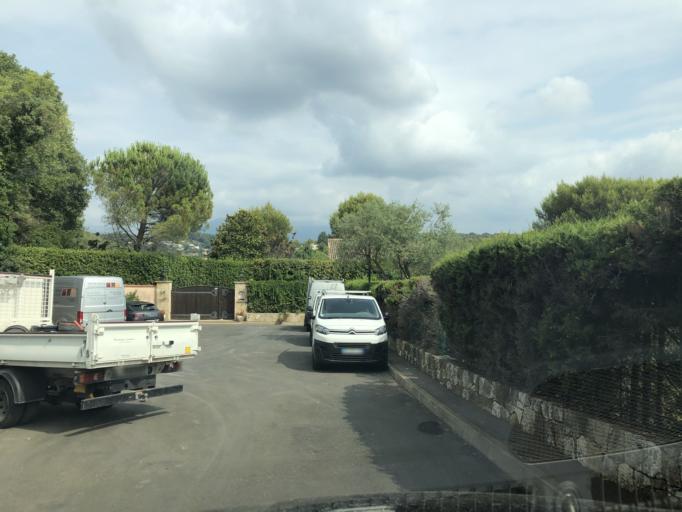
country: FR
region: Provence-Alpes-Cote d'Azur
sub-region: Departement des Alpes-Maritimes
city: Biot
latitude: 43.6277
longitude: 7.0849
